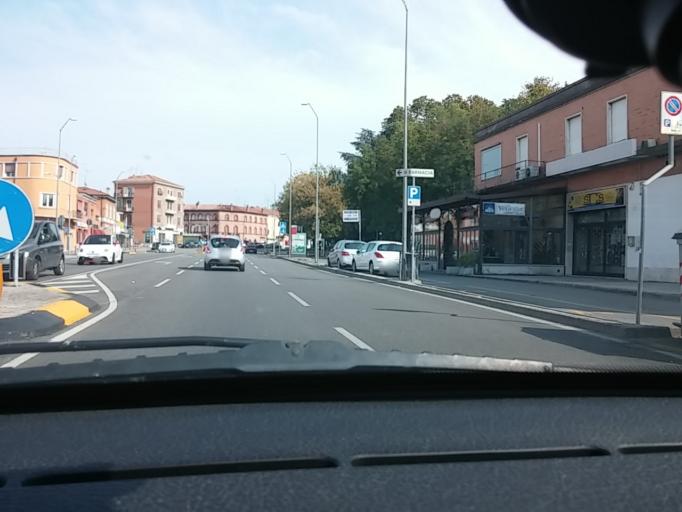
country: IT
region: Emilia-Romagna
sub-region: Provincia di Ferrara
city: Ferrara
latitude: 44.8453
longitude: 11.6064
